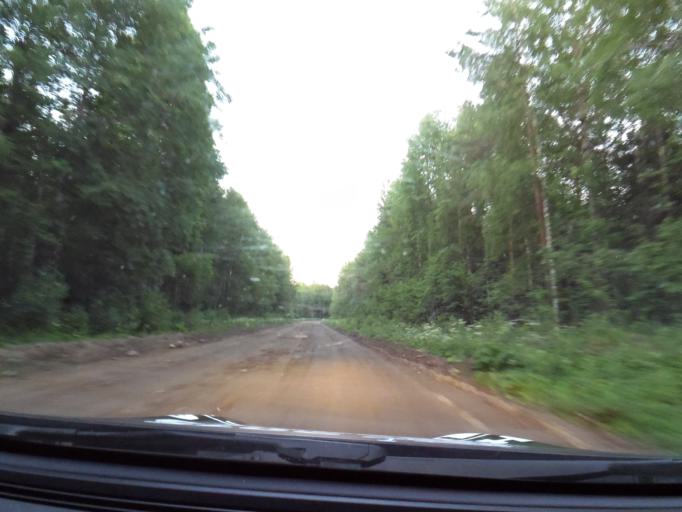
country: RU
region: Leningrad
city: Voznesen'ye
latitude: 60.8543
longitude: 35.8793
